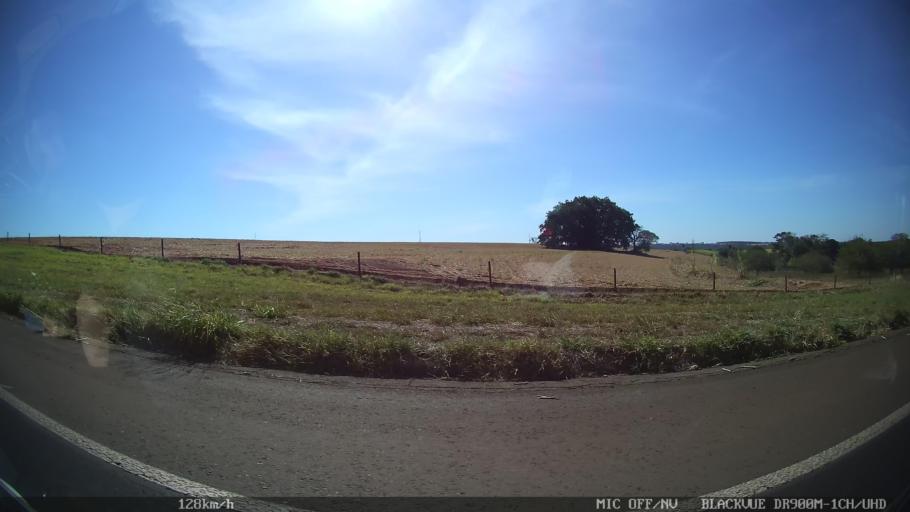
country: BR
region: Sao Paulo
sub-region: Olimpia
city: Olimpia
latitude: -20.6235
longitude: -48.7759
